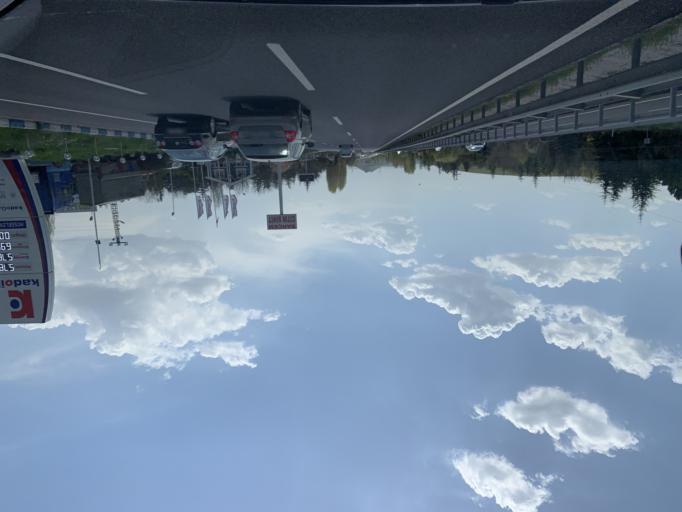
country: TR
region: Ankara
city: Etimesgut
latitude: 39.7969
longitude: 32.5345
